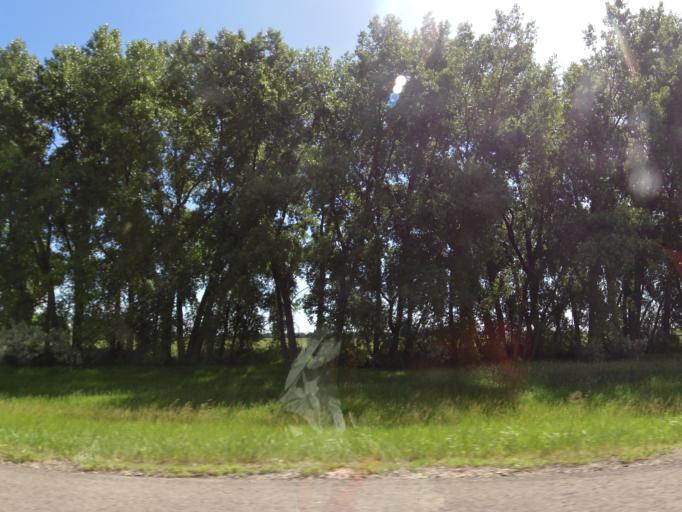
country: US
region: North Dakota
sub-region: Traill County
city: Hillsboro
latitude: 47.6615
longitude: -97.0803
